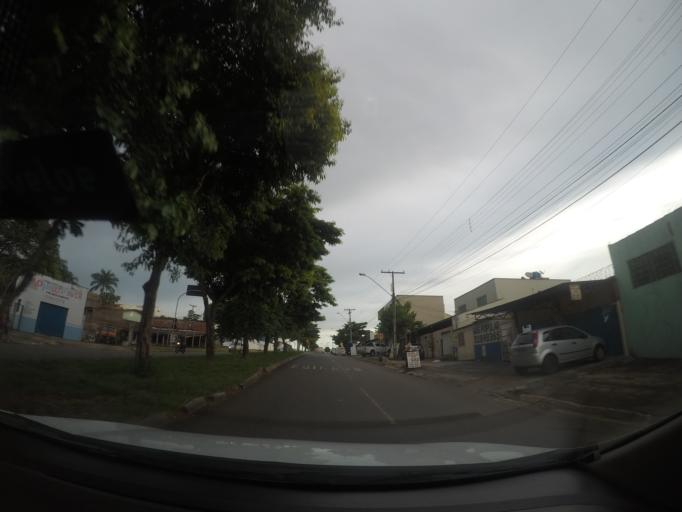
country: BR
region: Goias
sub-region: Goiania
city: Goiania
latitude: -16.7390
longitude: -49.3130
